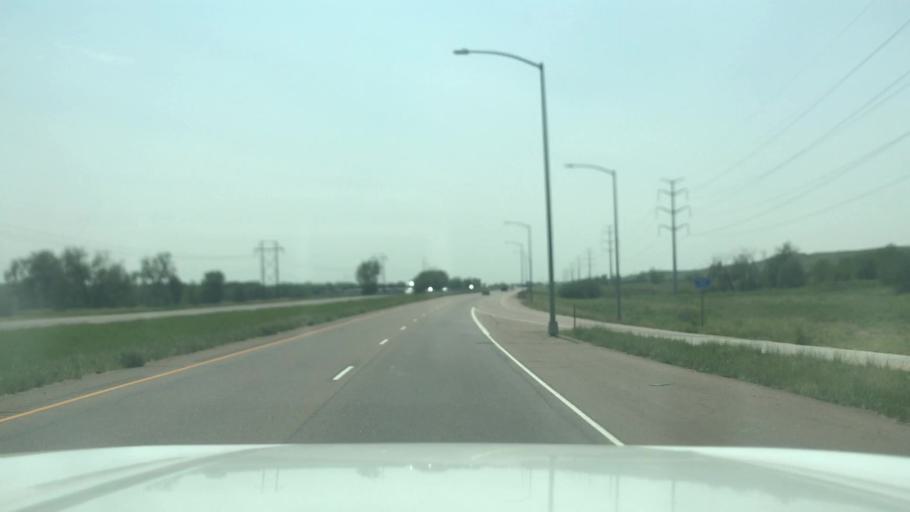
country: US
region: Colorado
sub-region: El Paso County
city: Security-Widefield
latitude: 38.7208
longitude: -104.7300
